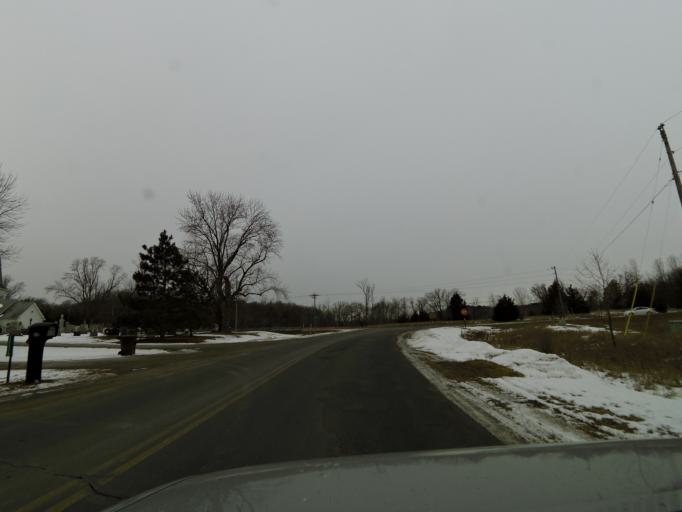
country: US
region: Minnesota
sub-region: Washington County
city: Lake Elmo
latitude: 44.9673
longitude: -92.8568
